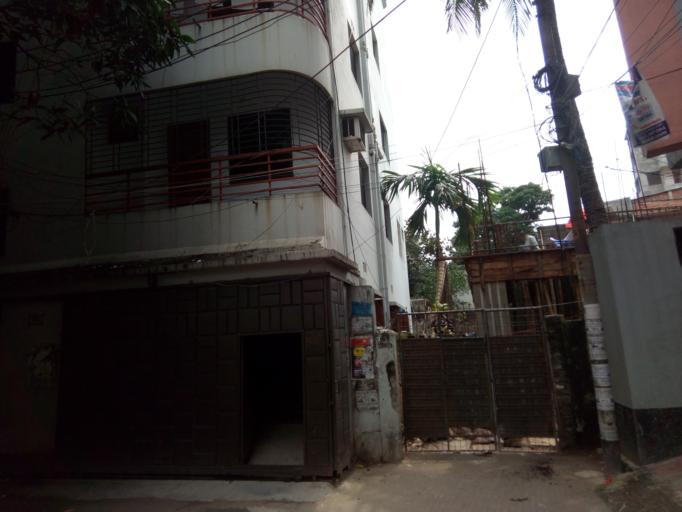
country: BD
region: Dhaka
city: Azimpur
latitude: 23.7445
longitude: 90.3659
